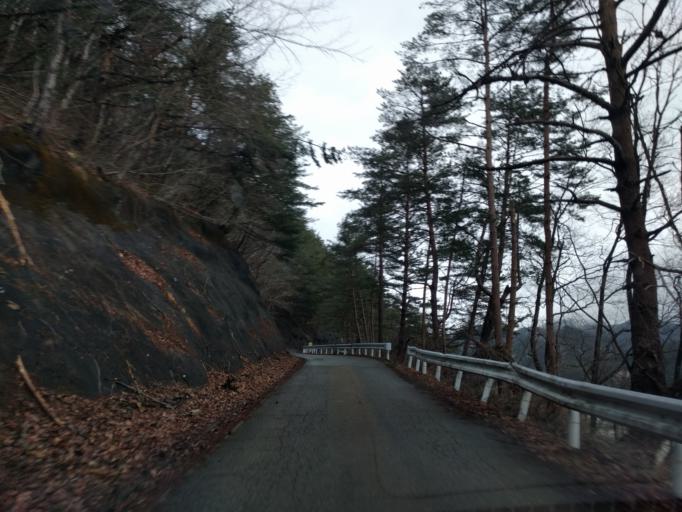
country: JP
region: Fukushima
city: Kitakata
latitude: 37.6827
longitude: 139.9258
